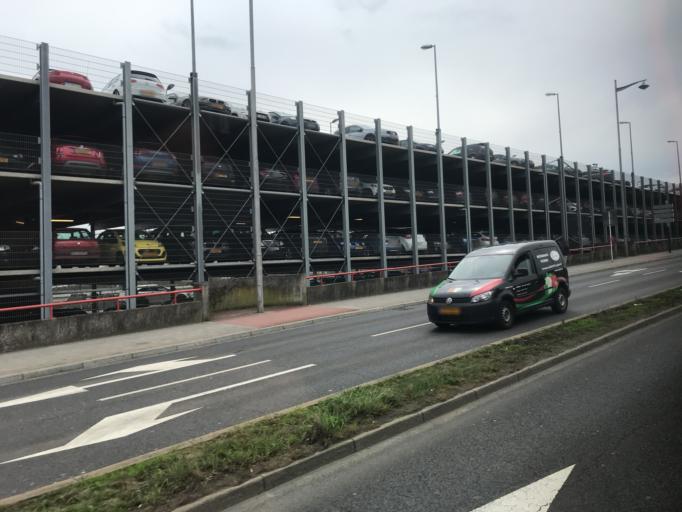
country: LU
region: Luxembourg
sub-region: Canton de Luxembourg
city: Luxembourg
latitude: 49.5980
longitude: 6.1323
